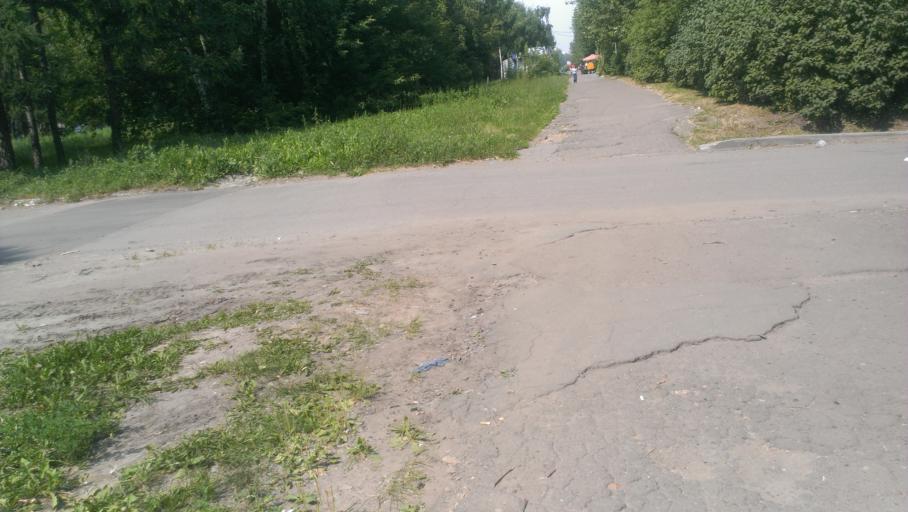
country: RU
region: Altai Krai
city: Novosilikatnyy
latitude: 53.3637
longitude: 83.6754
